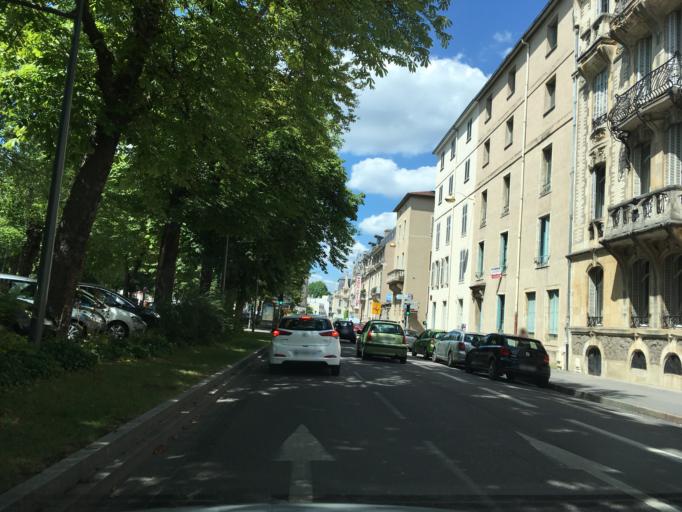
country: FR
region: Lorraine
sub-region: Departement de Meurthe-et-Moselle
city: Maxeville
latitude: 48.6964
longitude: 6.1761
